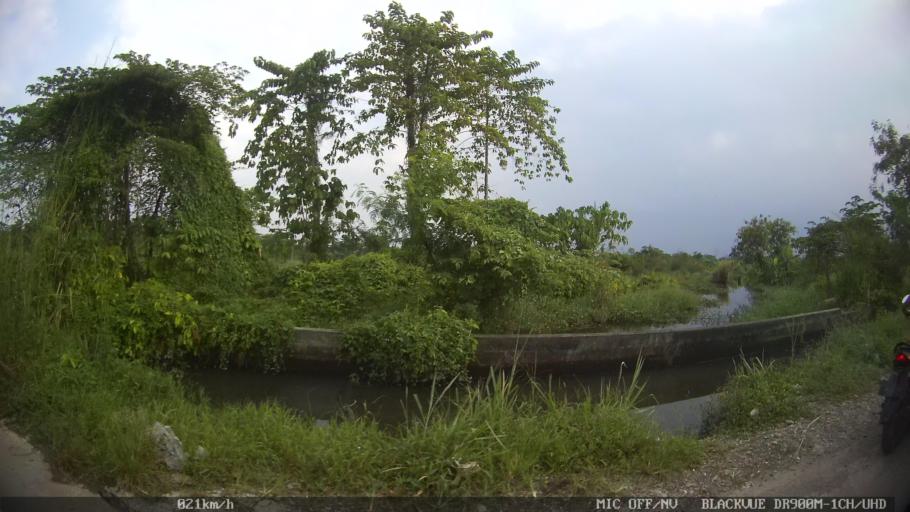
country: ID
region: North Sumatra
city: Medan
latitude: 3.6057
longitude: 98.7318
